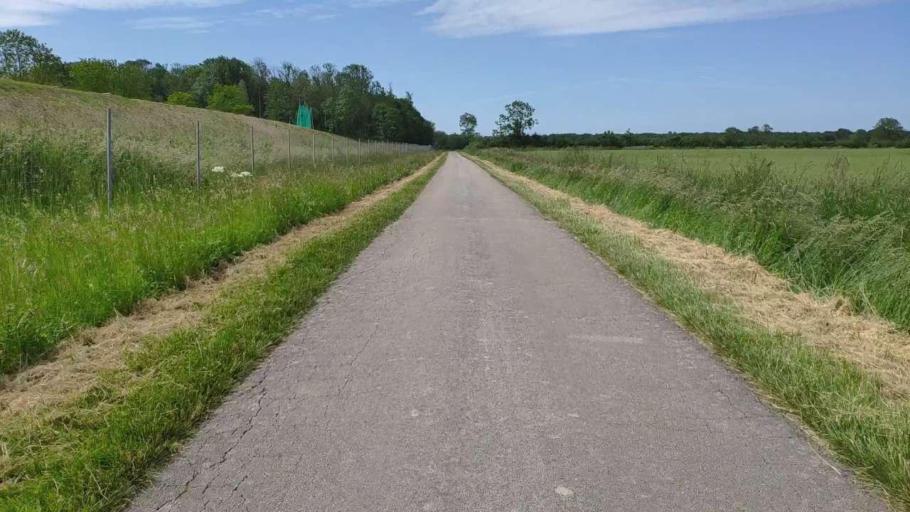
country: FR
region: Franche-Comte
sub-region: Departement du Jura
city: Bletterans
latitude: 46.6855
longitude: 5.4281
